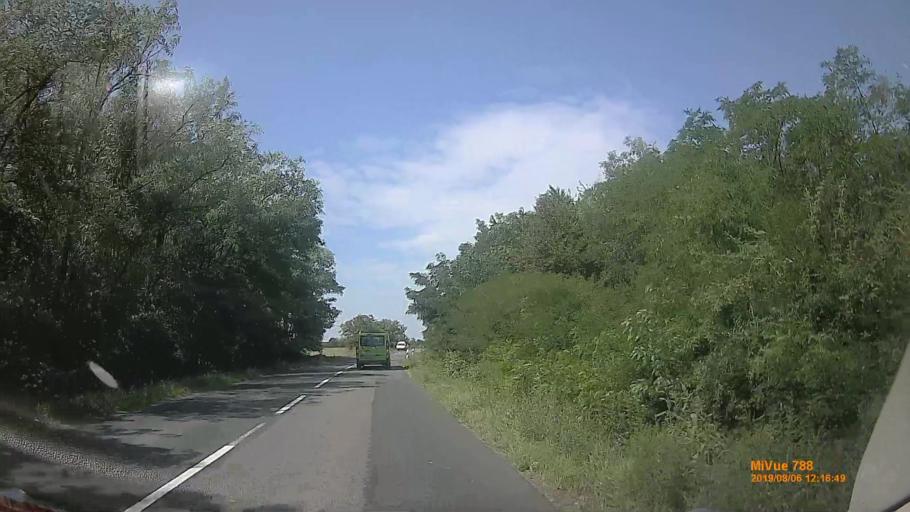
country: HU
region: Vas
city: Vep
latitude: 47.1583
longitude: 16.8000
